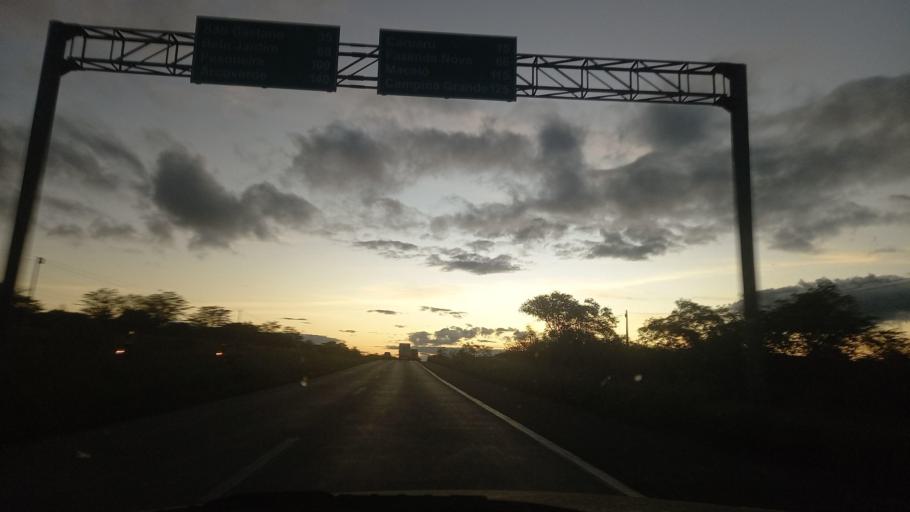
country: BR
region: Pernambuco
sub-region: Bezerros
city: Bezerros
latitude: -8.2977
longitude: -35.8599
